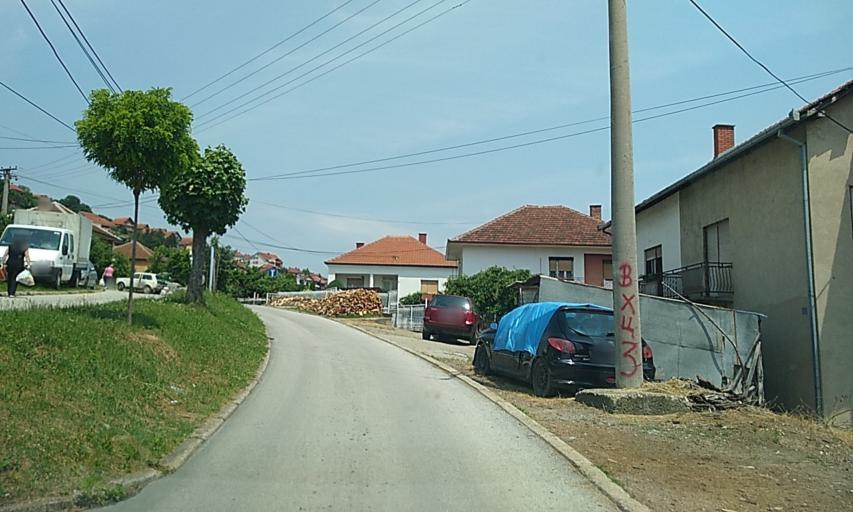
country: RS
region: Central Serbia
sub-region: Pcinjski Okrug
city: Vladicin Han
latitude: 42.7135
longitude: 22.0626
